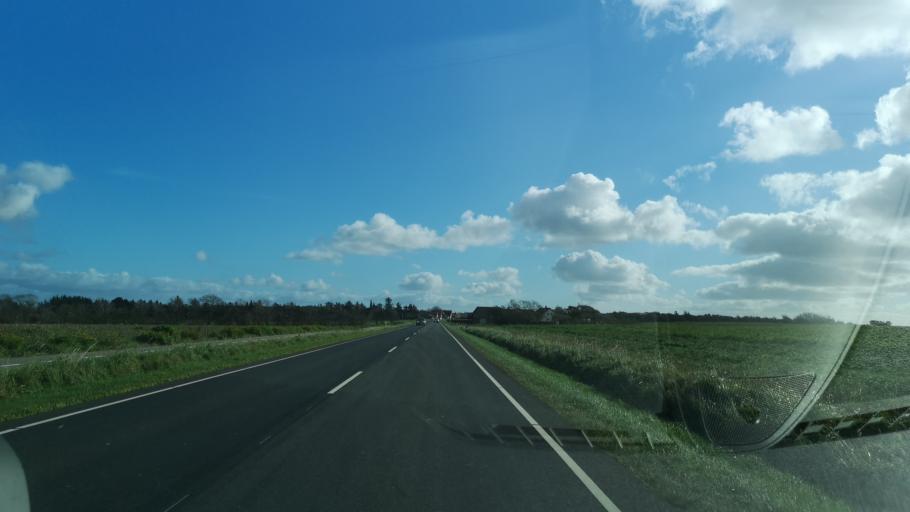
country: DK
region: South Denmark
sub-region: Varde Kommune
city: Oksbol
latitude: 55.7172
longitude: 8.2947
